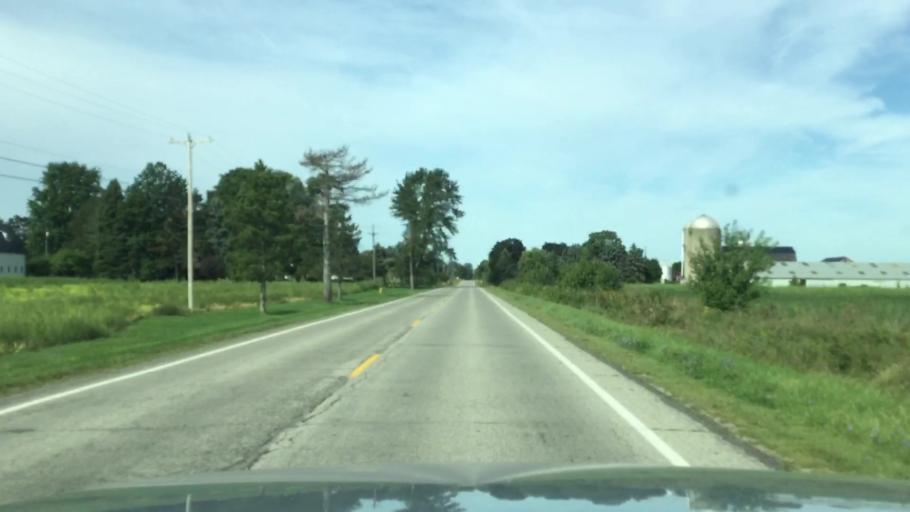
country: US
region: Michigan
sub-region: Genesee County
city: Montrose
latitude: 43.1179
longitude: -83.9045
